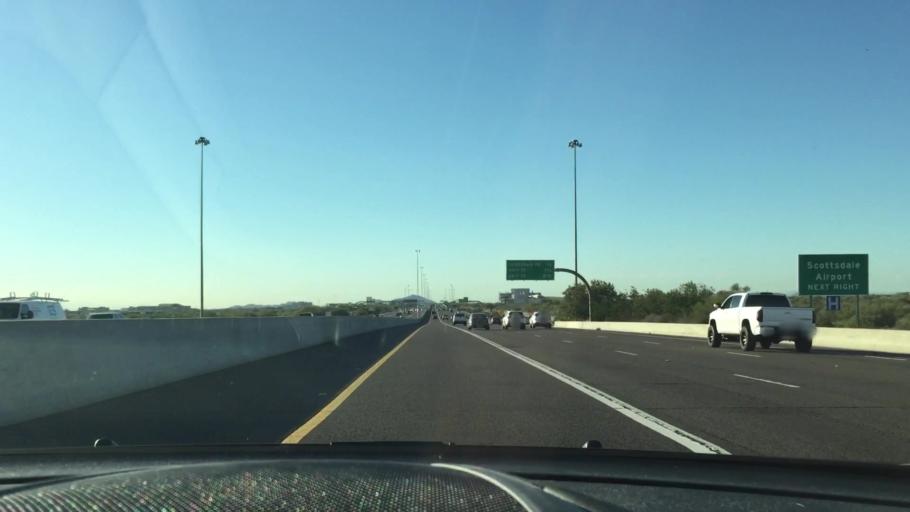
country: US
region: Arizona
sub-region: Maricopa County
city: Paradise Valley
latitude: 33.6502
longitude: -111.9067
